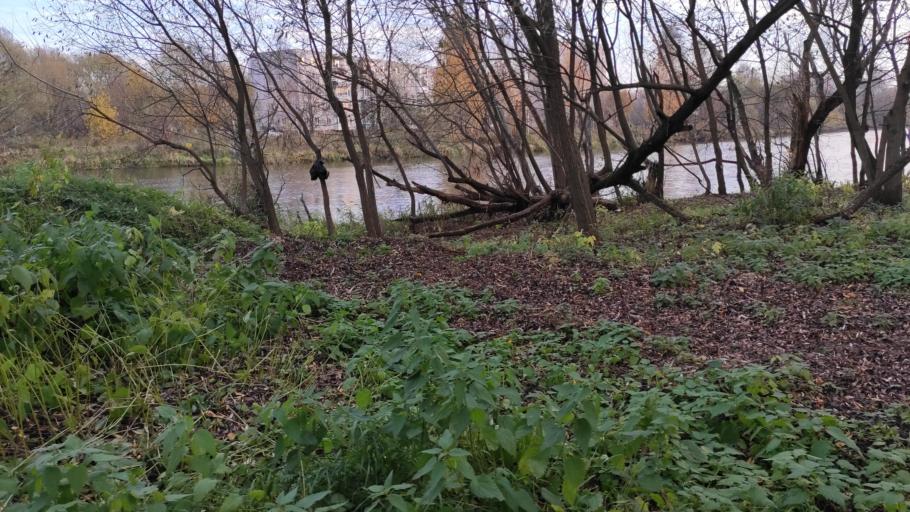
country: RU
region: Moskovskaya
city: Noginsk
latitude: 55.8677
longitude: 38.4509
